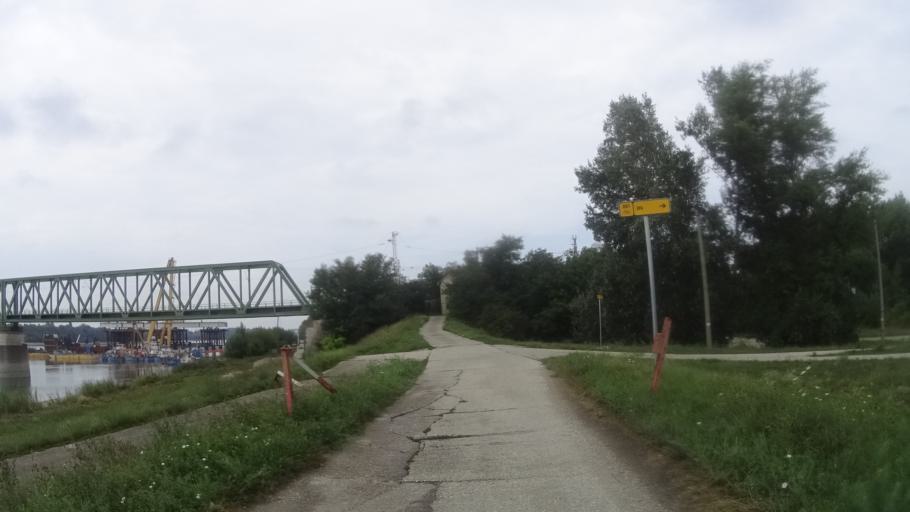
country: SK
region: Nitriansky
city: Komarno
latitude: 47.7591
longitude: 18.0886
